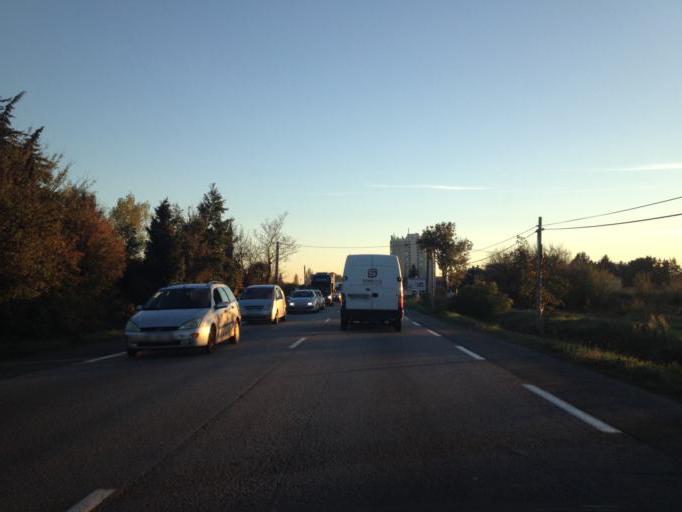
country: FR
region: Rhone-Alpes
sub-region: Departement de la Drome
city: Ancone
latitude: 44.5623
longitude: 4.7312
